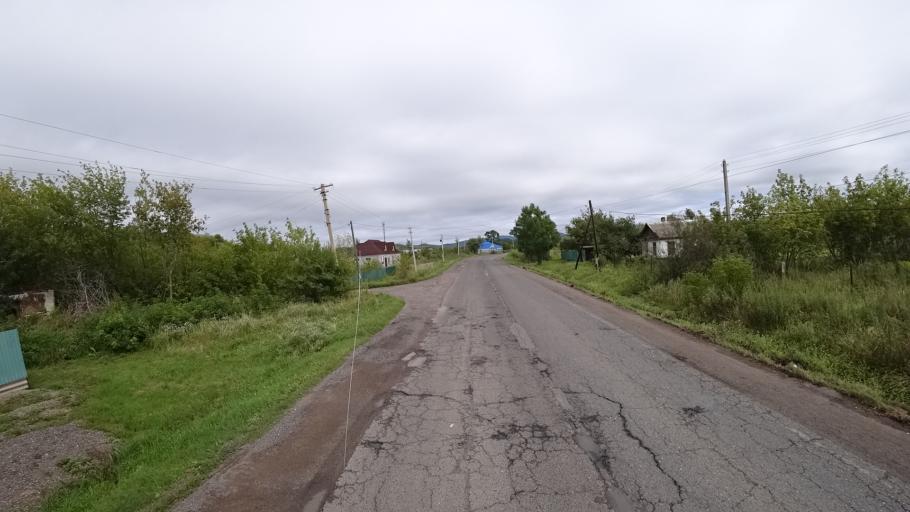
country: RU
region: Primorskiy
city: Monastyrishche
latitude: 44.2033
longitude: 132.4695
